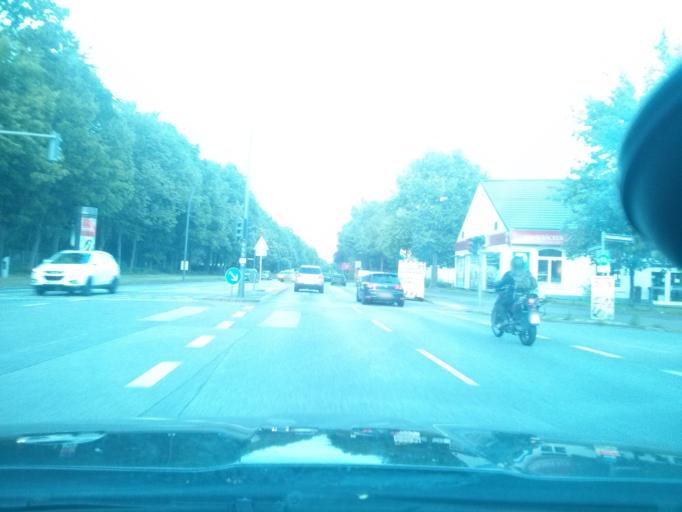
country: DE
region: Schleswig-Holstein
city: Halstenbek
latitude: 53.5763
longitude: 9.8230
